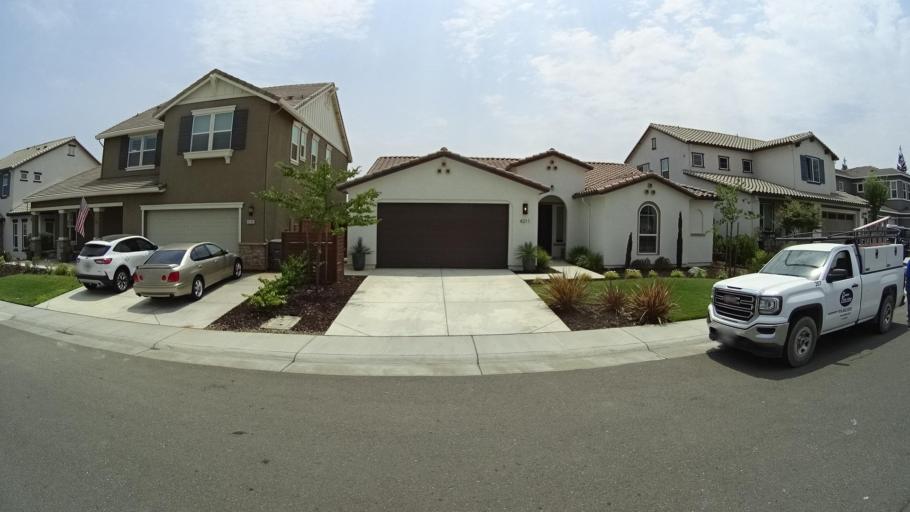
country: US
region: California
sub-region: Placer County
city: Loomis
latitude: 38.8007
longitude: -121.2003
